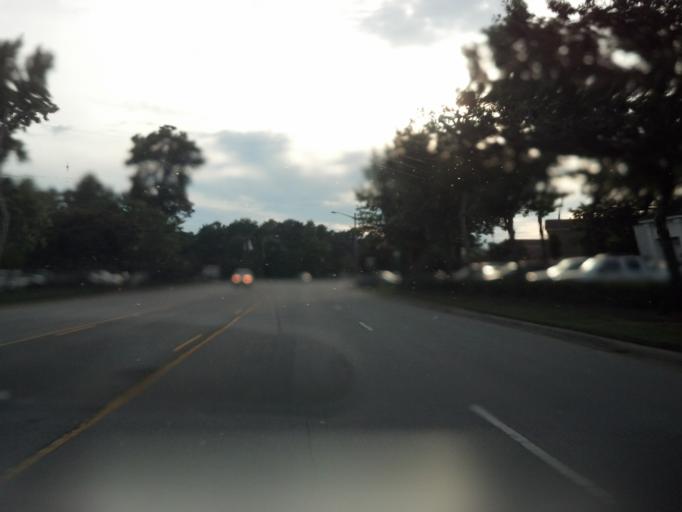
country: US
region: North Carolina
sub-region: Pitt County
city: Windsor
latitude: 35.5816
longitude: -77.3691
